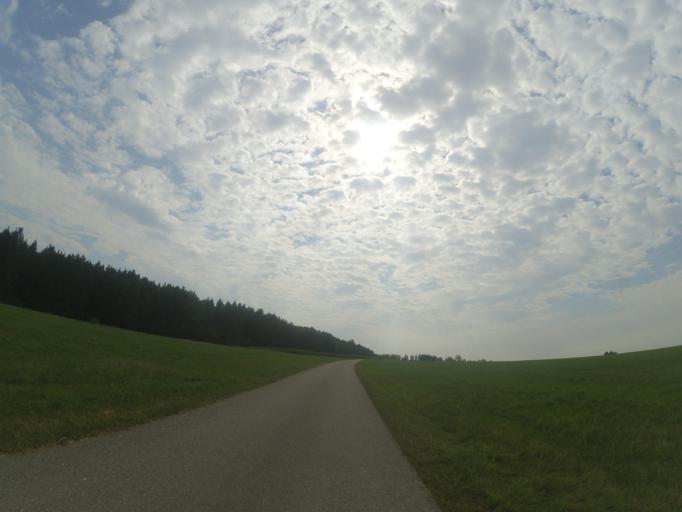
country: DE
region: Baden-Wuerttemberg
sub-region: Tuebingen Region
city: Lonsee
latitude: 48.4994
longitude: 9.8948
